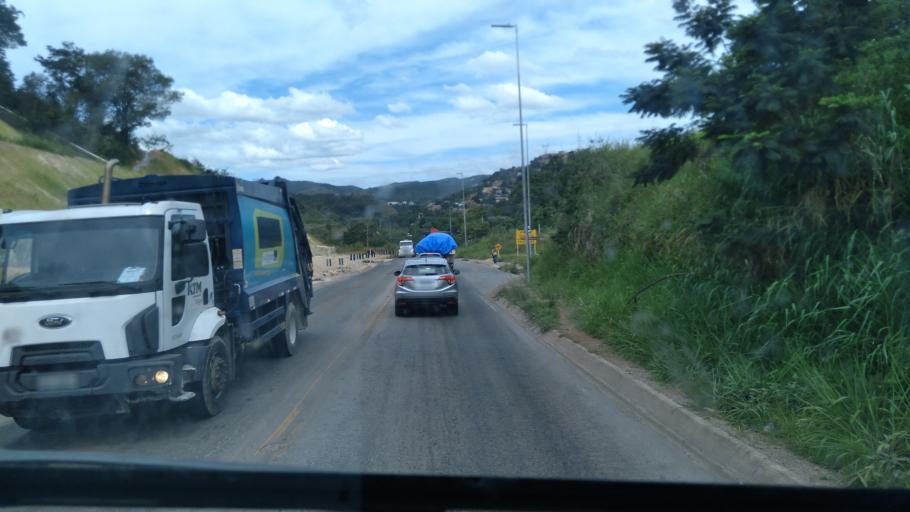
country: BR
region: Minas Gerais
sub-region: Belo Horizonte
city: Belo Horizonte
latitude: -19.8769
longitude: -43.8610
